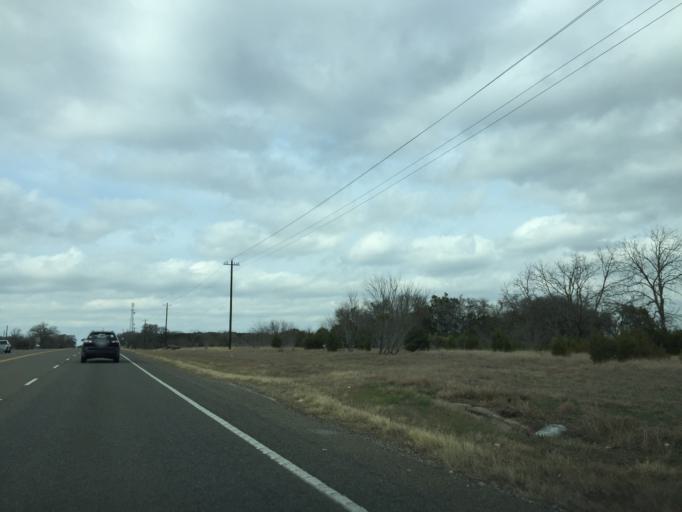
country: US
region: Texas
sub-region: Burnet County
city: Marble Falls
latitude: 30.4762
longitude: -98.1876
